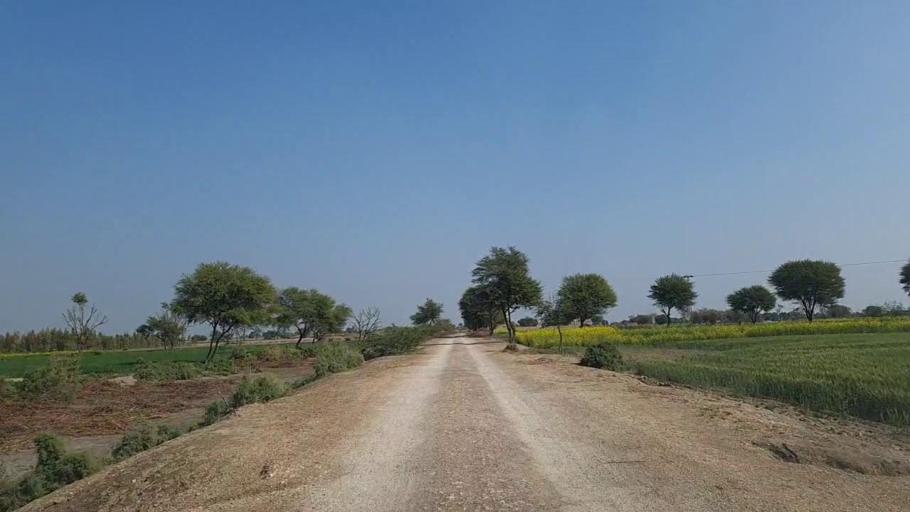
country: PK
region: Sindh
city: Jam Sahib
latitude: 26.2540
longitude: 68.5684
